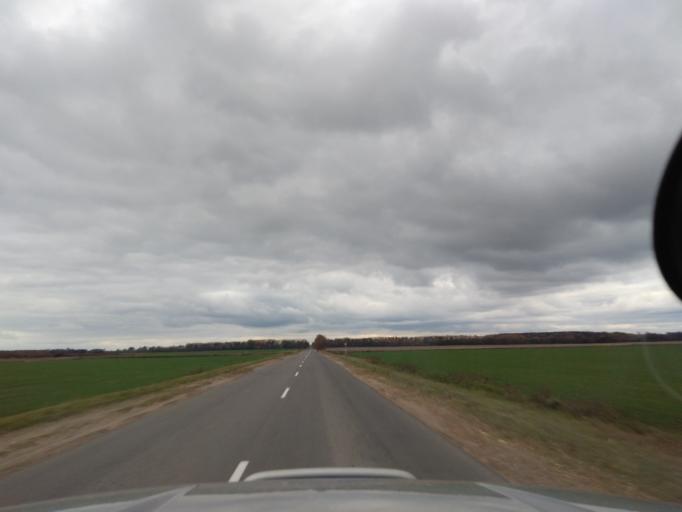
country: BY
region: Minsk
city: Slutsk
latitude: 53.2111
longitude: 27.3657
